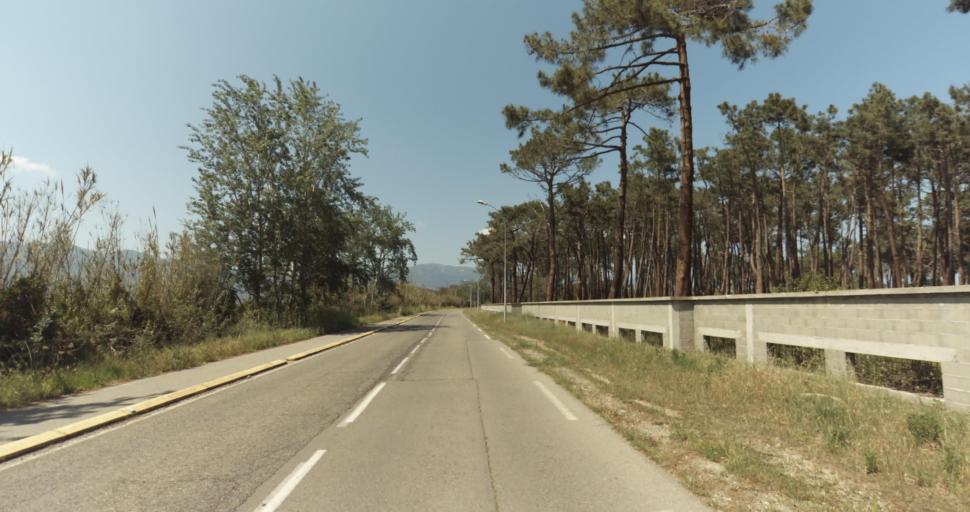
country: FR
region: Corsica
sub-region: Departement de la Haute-Corse
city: Biguglia
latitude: 42.6194
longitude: 9.4755
